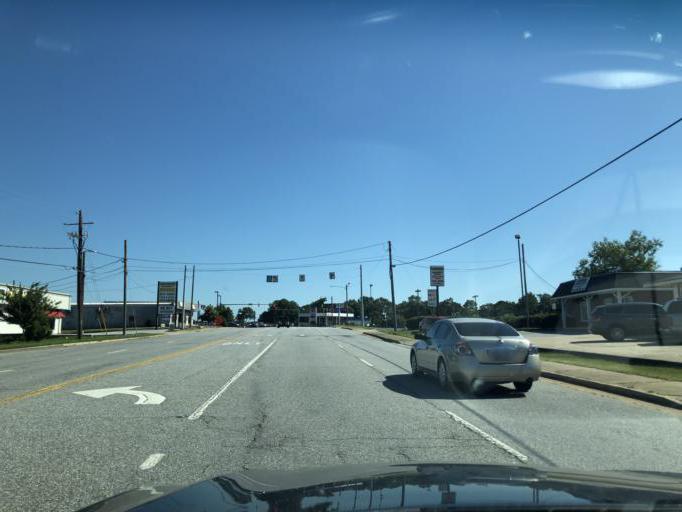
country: US
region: Georgia
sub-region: Muscogee County
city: Columbus
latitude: 32.5084
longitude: -84.9536
